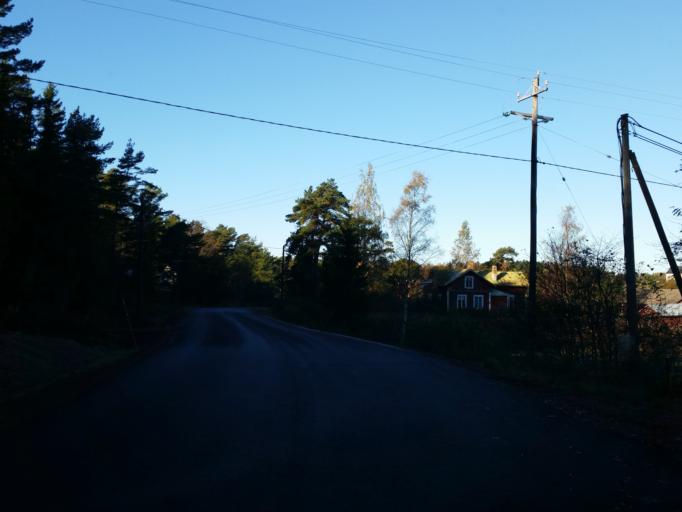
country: AX
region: Alands landsbygd
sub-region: Sund
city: Sund
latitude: 60.2299
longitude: 20.0890
